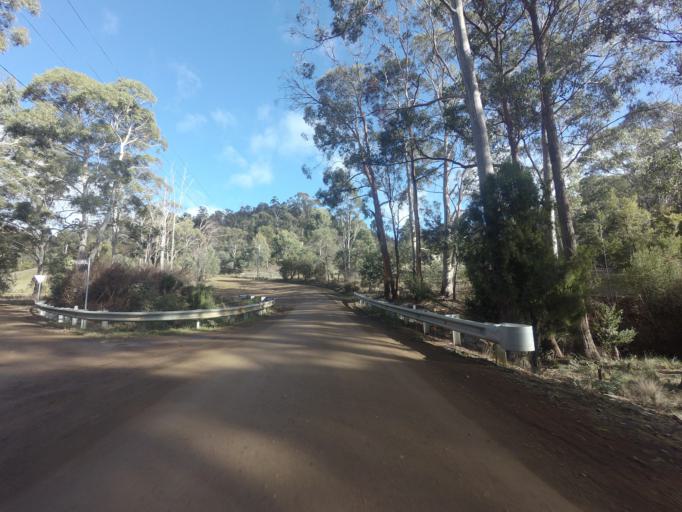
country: AU
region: Tasmania
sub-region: Derwent Valley
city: New Norfolk
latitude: -42.8164
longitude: 147.1286
